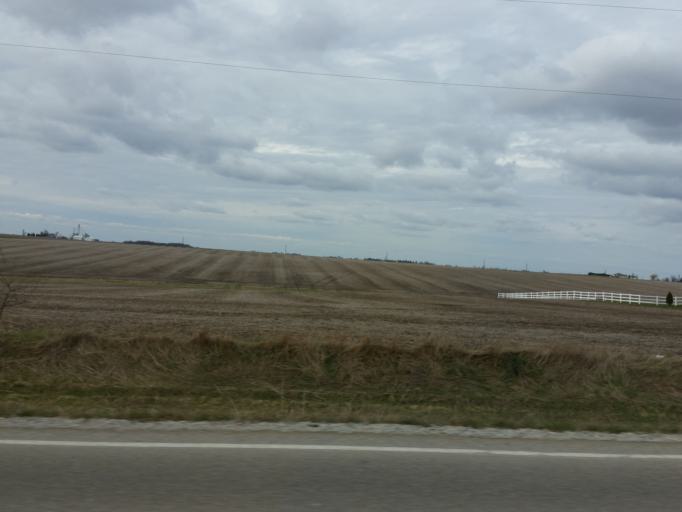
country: US
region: Iowa
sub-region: Black Hawk County
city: Elk Run Heights
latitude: 42.5703
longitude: -92.2279
